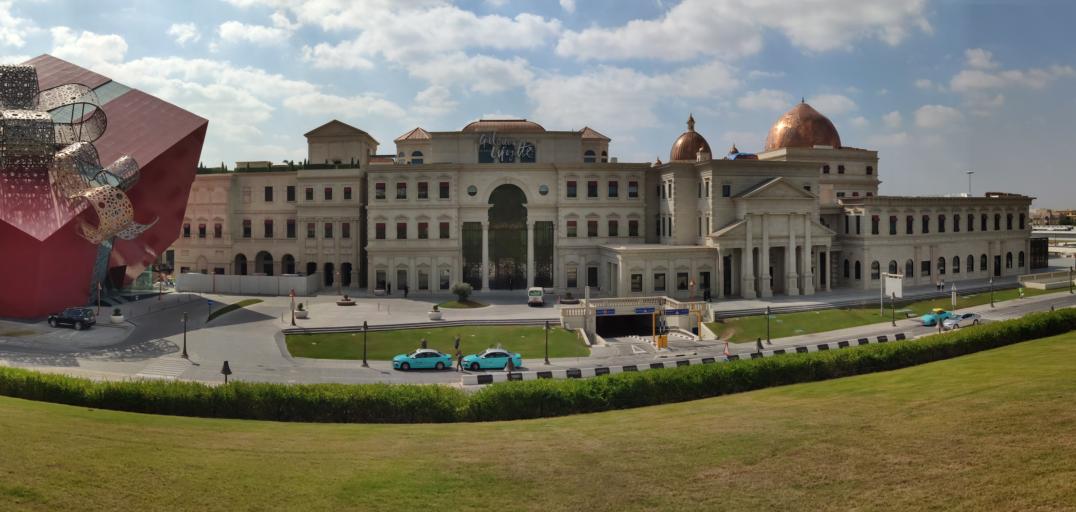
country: QA
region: Baladiyat ad Dawhah
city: Doha
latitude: 25.3627
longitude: 51.5240
